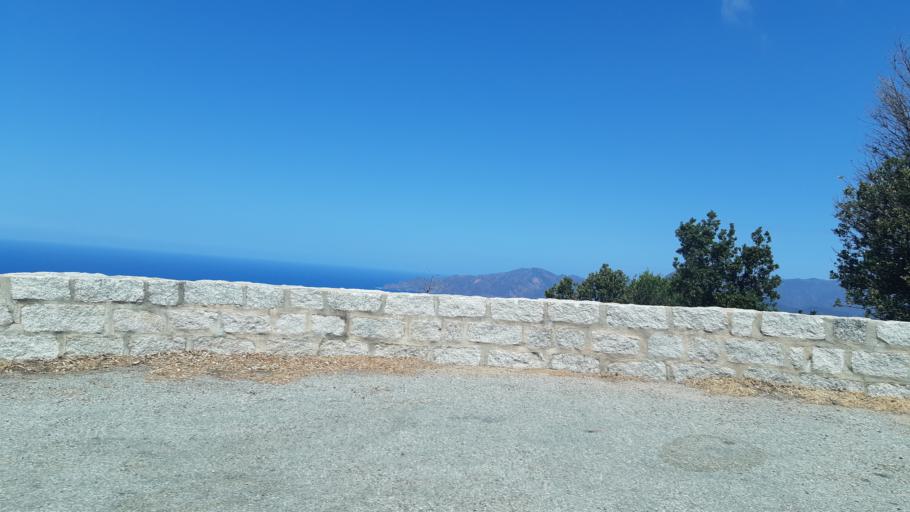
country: FR
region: Corsica
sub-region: Departement de la Corse-du-Sud
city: Cargese
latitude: 42.2444
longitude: 8.6212
